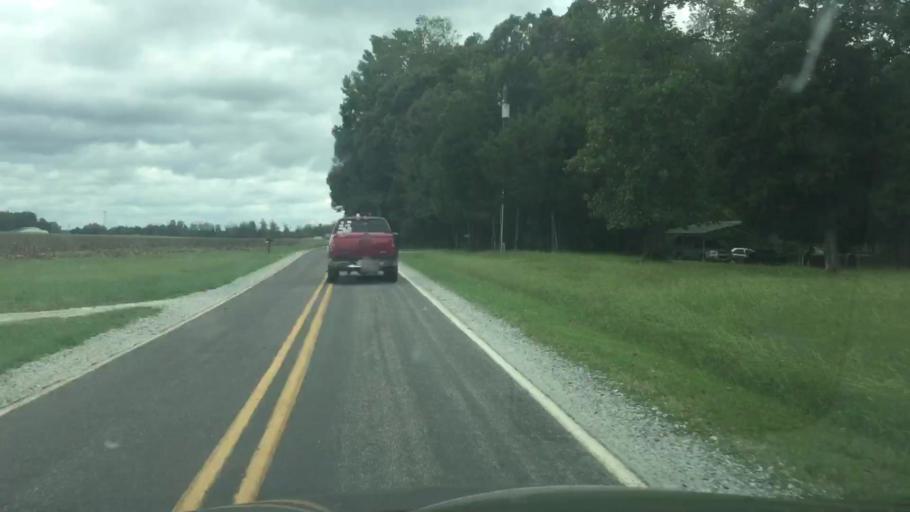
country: US
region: North Carolina
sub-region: Rowan County
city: China Grove
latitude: 35.6478
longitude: -80.6628
